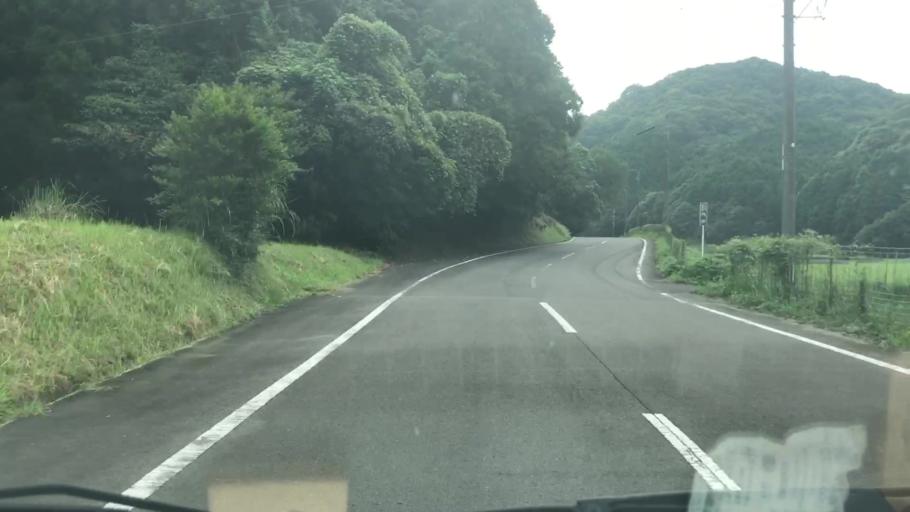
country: JP
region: Saga Prefecture
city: Takeocho-takeo
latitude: 33.2264
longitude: 129.9848
